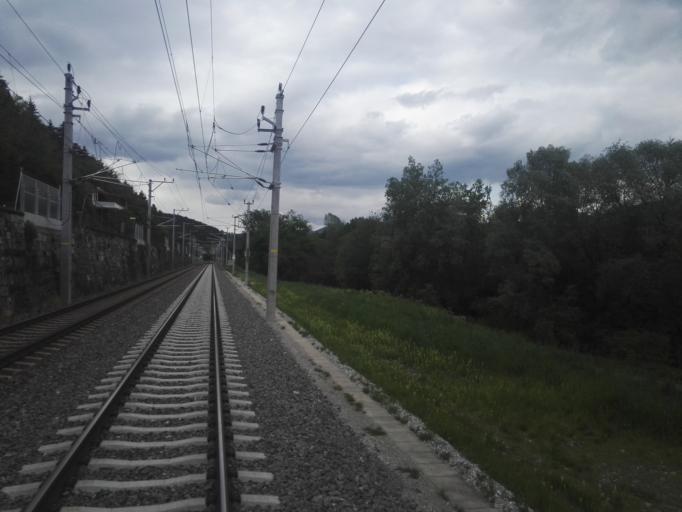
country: AT
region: Styria
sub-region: Politischer Bezirk Graz-Umgebung
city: Deutschfeistritz
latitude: 47.1679
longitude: 15.3191
